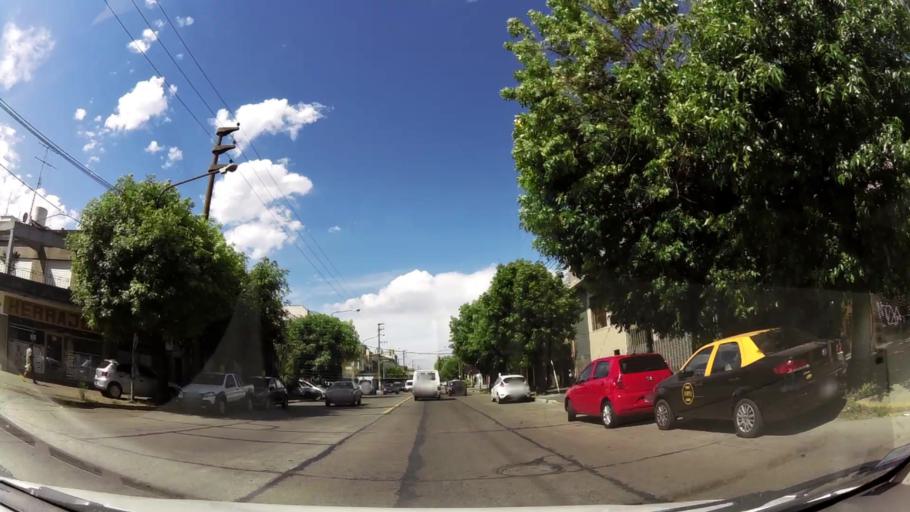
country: AR
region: Buenos Aires
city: San Justo
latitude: -34.6623
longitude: -58.5363
